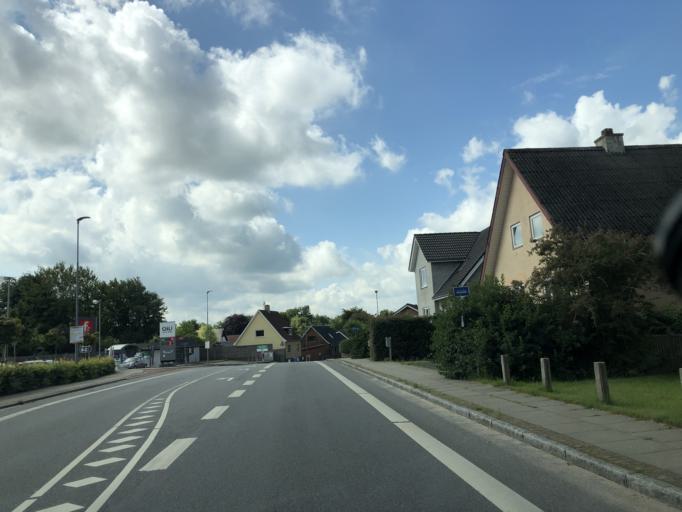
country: DK
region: Central Jutland
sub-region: Ikast-Brande Kommune
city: Brande
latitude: 55.9443
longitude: 9.1360
